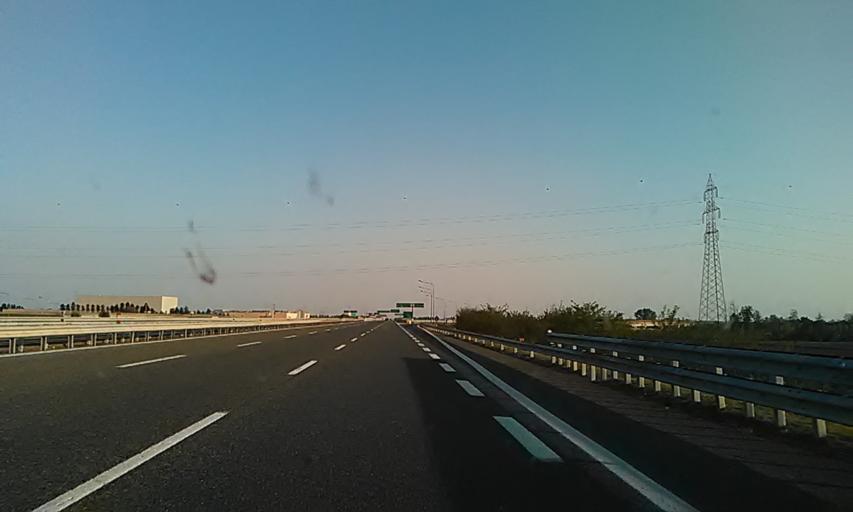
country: IT
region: Piedmont
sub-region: Provincia di Novara
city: Vicolungo
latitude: 45.4709
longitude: 8.4484
